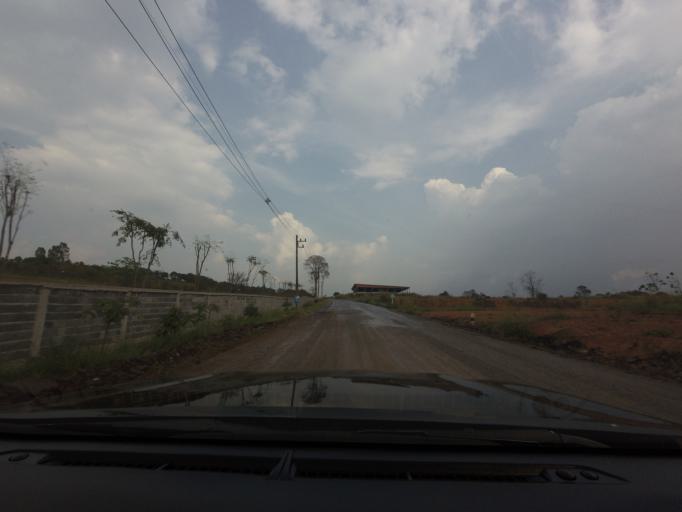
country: TH
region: Nakhon Ratchasima
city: Wang Nam Khiao
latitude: 14.4105
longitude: 101.7484
